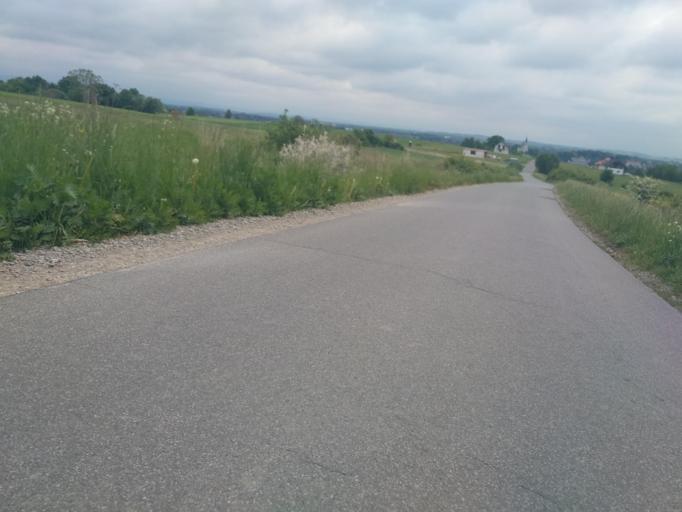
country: PL
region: Subcarpathian Voivodeship
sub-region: Powiat krosnienski
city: Chorkowka
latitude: 49.6710
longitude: 21.6693
